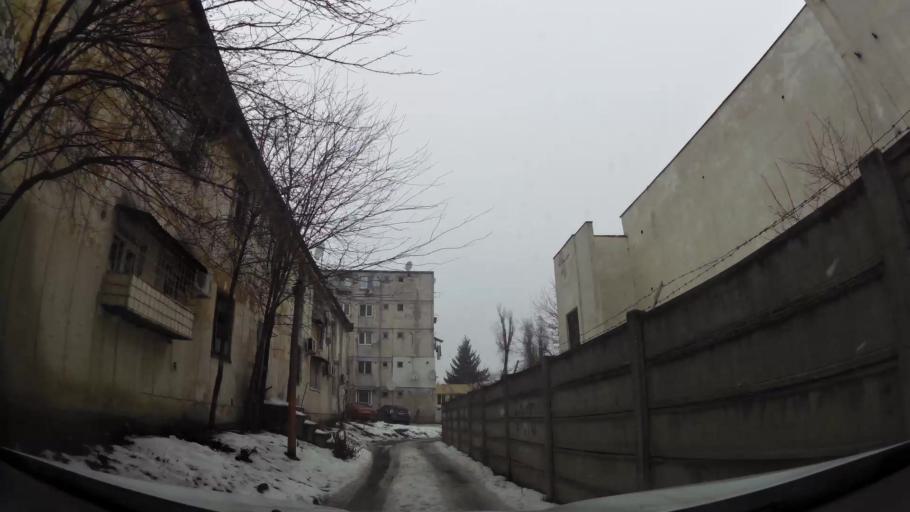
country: RO
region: Ilfov
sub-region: Comuna Chiajna
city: Rosu
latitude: 44.4317
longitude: 25.9896
